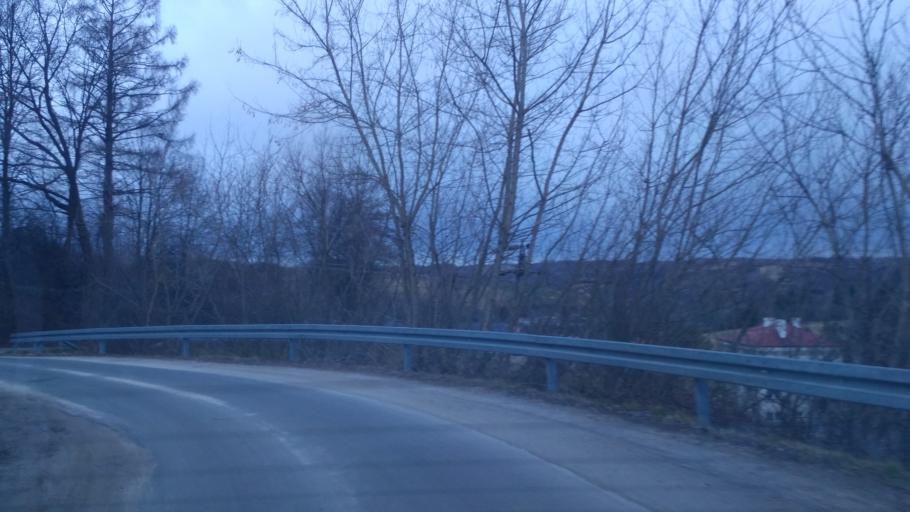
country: PL
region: Subcarpathian Voivodeship
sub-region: Powiat rzeszowski
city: Blazowa
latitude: 49.8890
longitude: 22.1076
